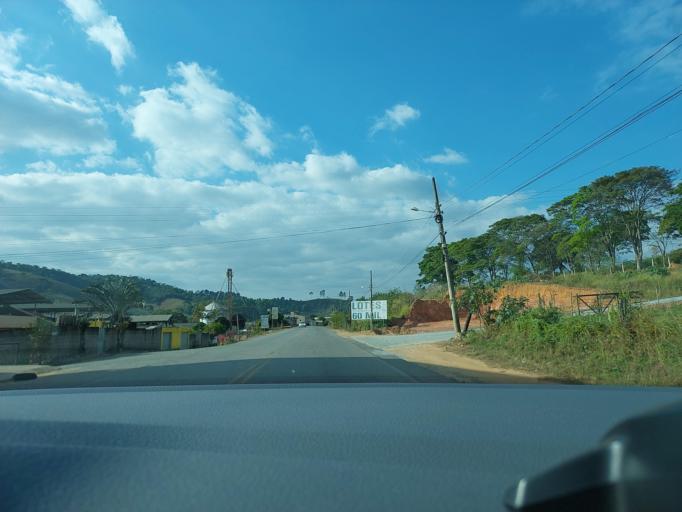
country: BR
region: Minas Gerais
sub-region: Vicosa
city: Vicosa
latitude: -20.8355
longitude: -42.7984
